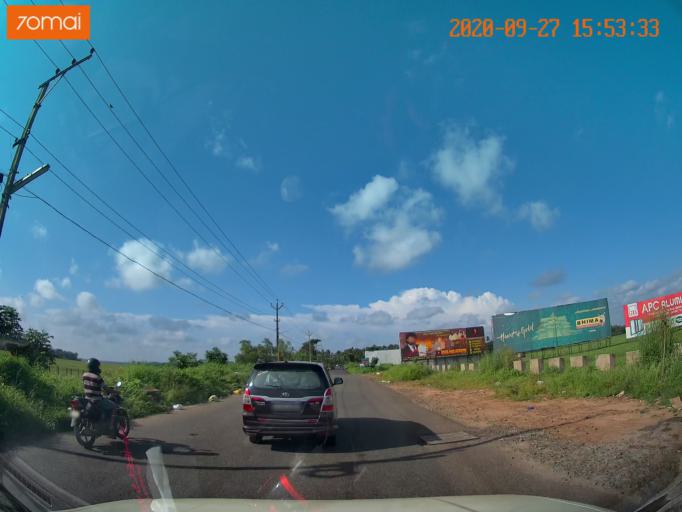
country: IN
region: Kerala
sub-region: Thrissur District
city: Trichur
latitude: 10.4995
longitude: 76.1658
